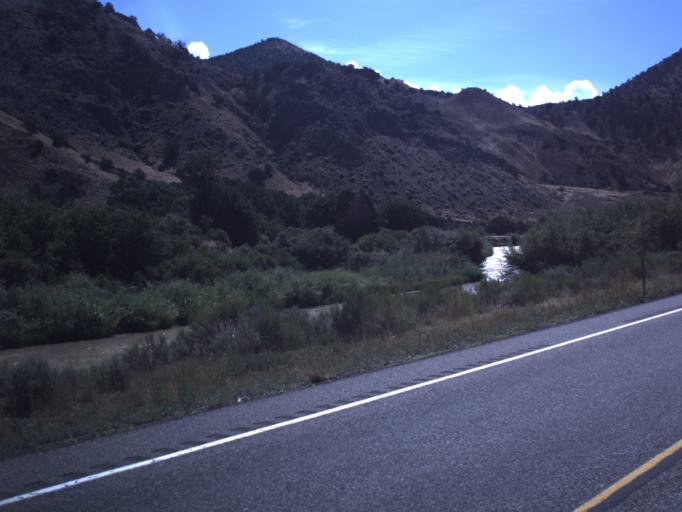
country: US
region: Utah
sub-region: Sevier County
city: Monroe
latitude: 38.5261
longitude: -112.2672
